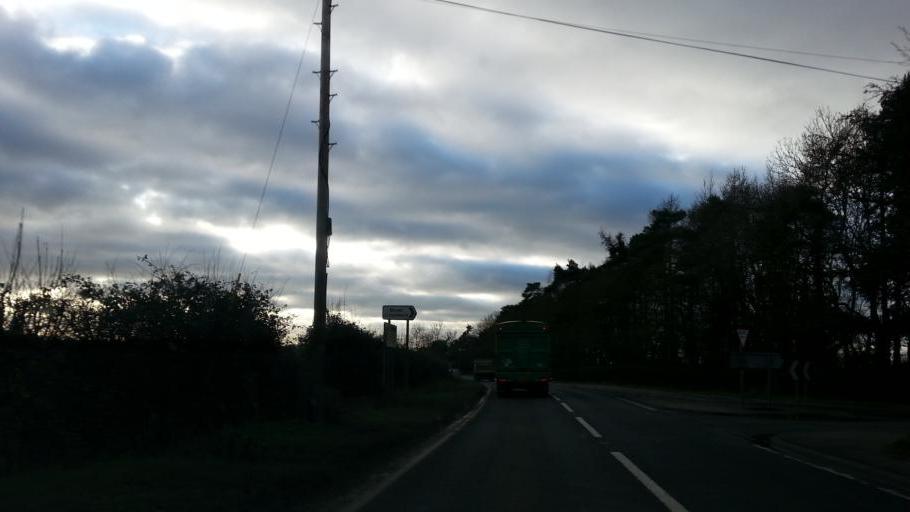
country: GB
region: England
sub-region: Suffolk
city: Great Barton
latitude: 52.2592
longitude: 0.7525
